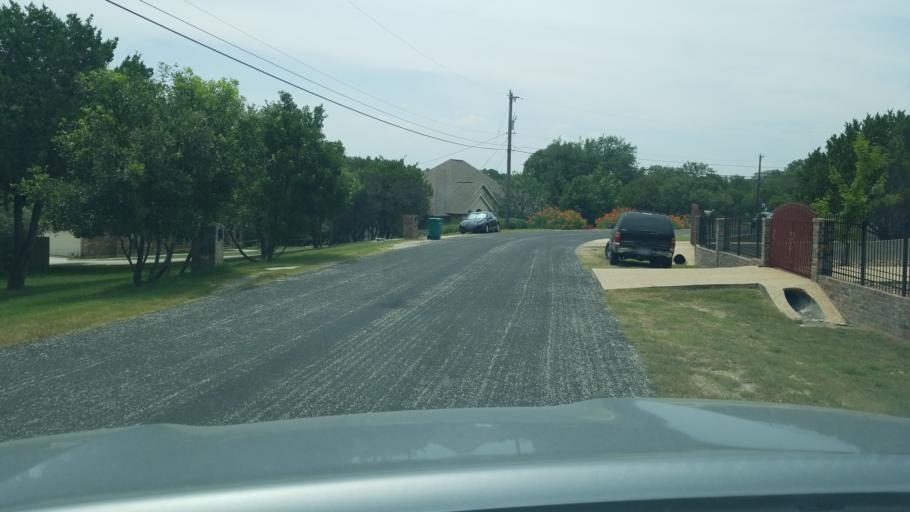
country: US
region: Texas
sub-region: Bexar County
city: Timberwood Park
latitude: 29.6877
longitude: -98.5098
